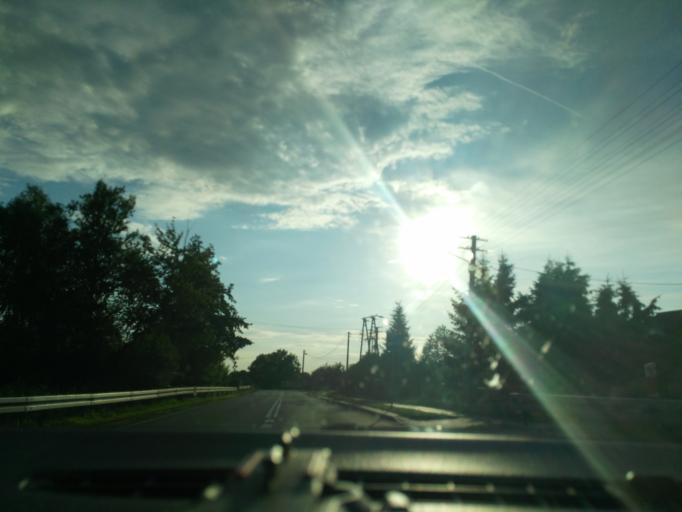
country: PL
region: Lublin Voivodeship
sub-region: Powiat krasnicki
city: Szastarka
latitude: 50.8253
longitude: 22.3133
